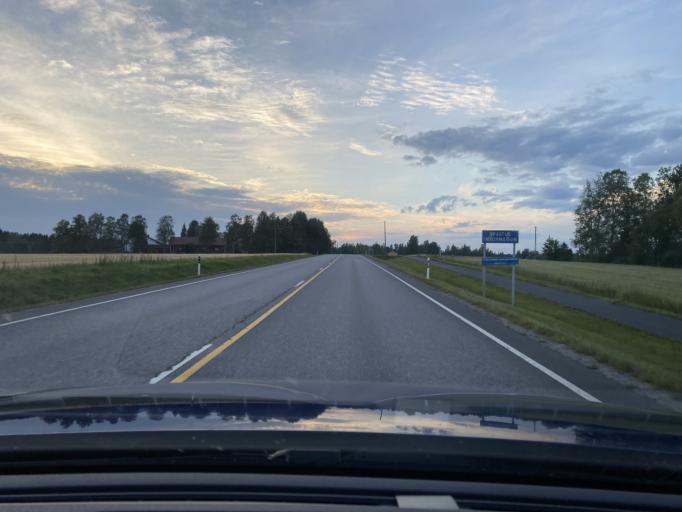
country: FI
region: Satakunta
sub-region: Pohjois-Satakunta
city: Kankaanpaeae
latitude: 61.7517
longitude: 22.5126
